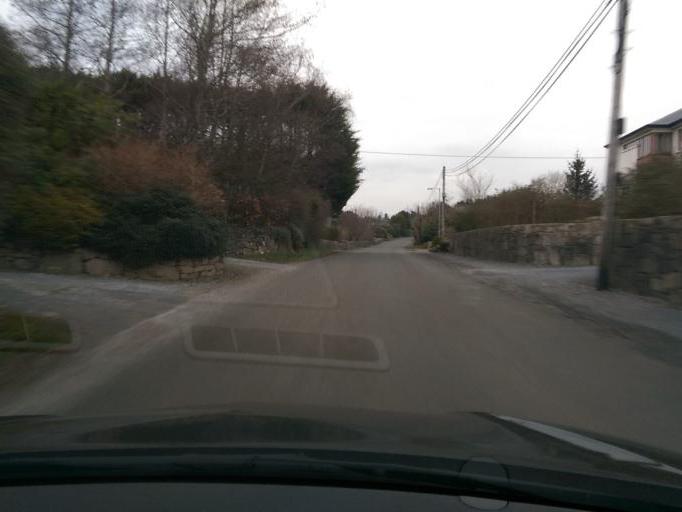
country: IE
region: Connaught
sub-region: County Galway
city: Bearna
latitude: 53.2548
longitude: -9.1535
